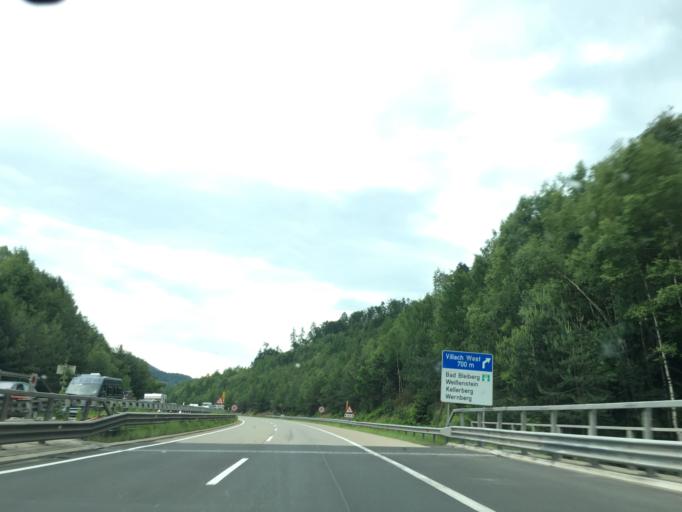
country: AT
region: Carinthia
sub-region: Villach Stadt
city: Villach
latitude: 46.6442
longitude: 13.7820
